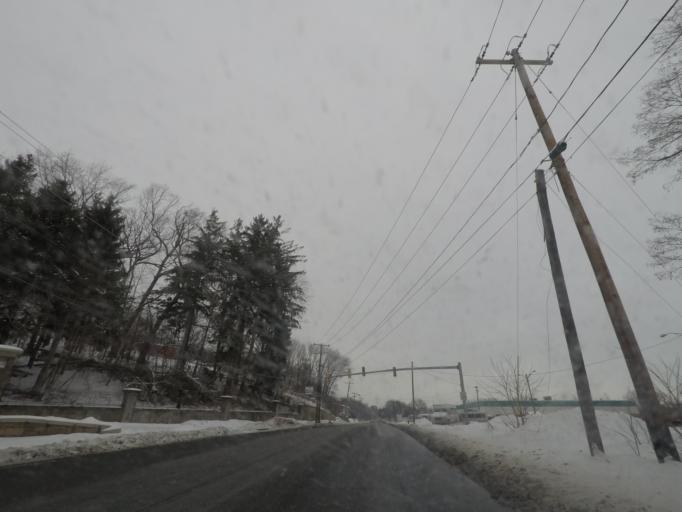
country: US
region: New York
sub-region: Albany County
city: Albany
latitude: 42.6279
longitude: -73.7672
